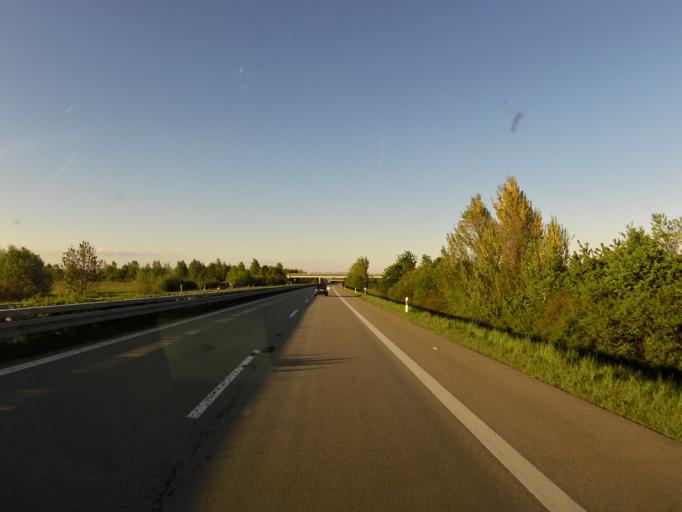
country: DE
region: Bavaria
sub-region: Lower Bavaria
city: Landau an der Isar
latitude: 48.7044
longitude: 12.6895
